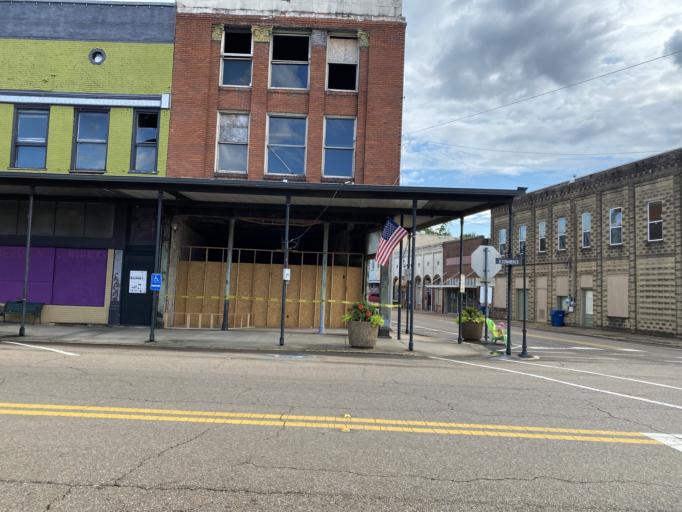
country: US
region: Mississippi
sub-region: Monroe County
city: Aberdeen
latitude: 33.8253
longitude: -88.5437
